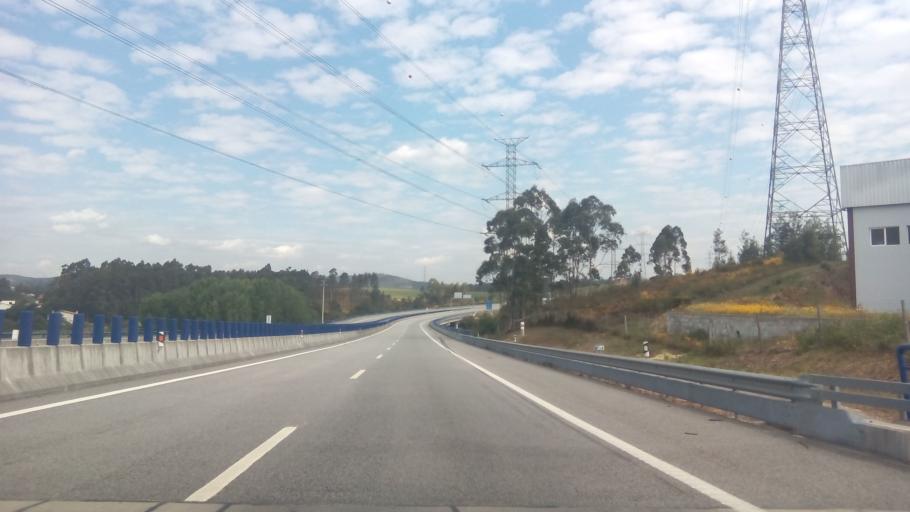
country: PT
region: Porto
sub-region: Valongo
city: Campo
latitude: 41.1871
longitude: -8.4549
